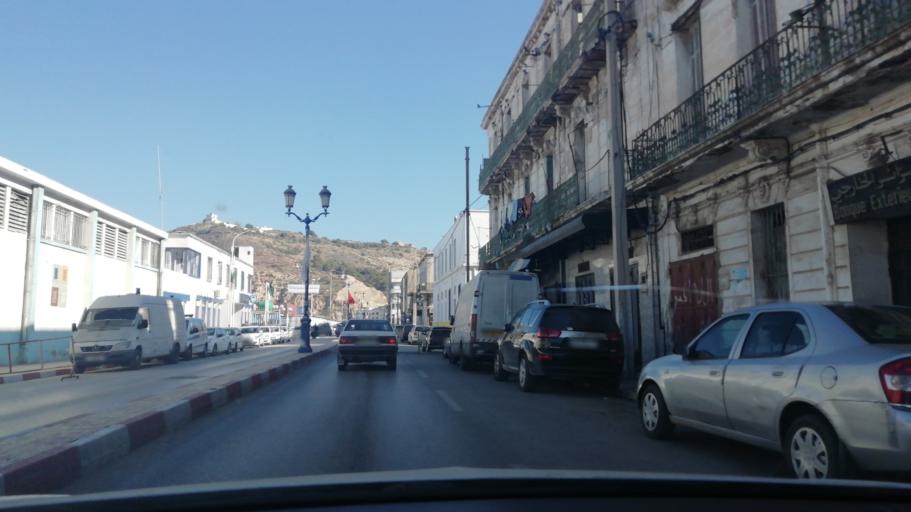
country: DZ
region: Tlemcen
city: Nedroma
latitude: 35.1007
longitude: -1.8607
